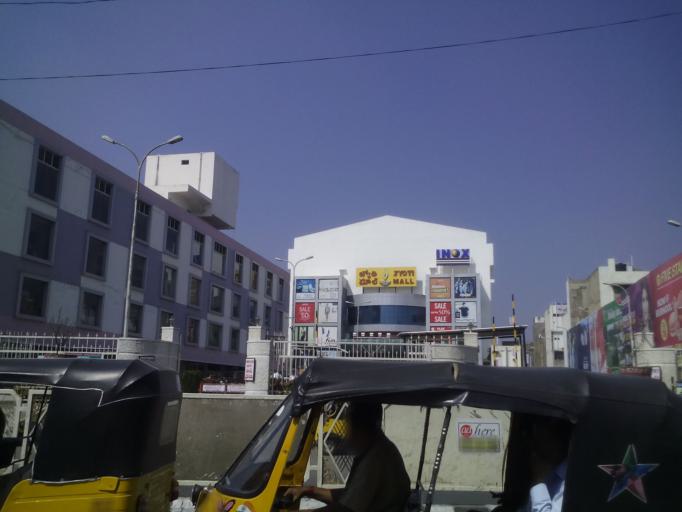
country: IN
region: Telangana
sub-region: Mahbubnagar
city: Alampur
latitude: 15.8293
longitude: 78.0404
